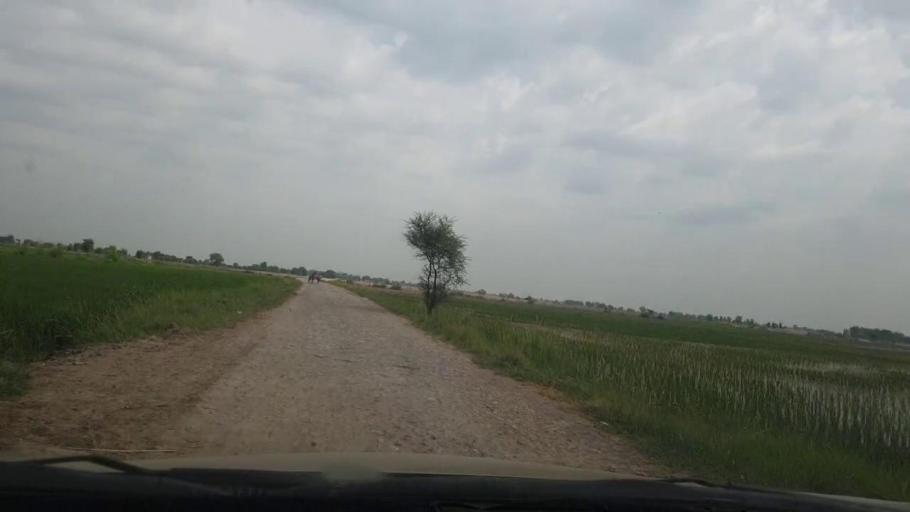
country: PK
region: Sindh
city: Ratodero
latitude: 27.7210
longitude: 68.2319
